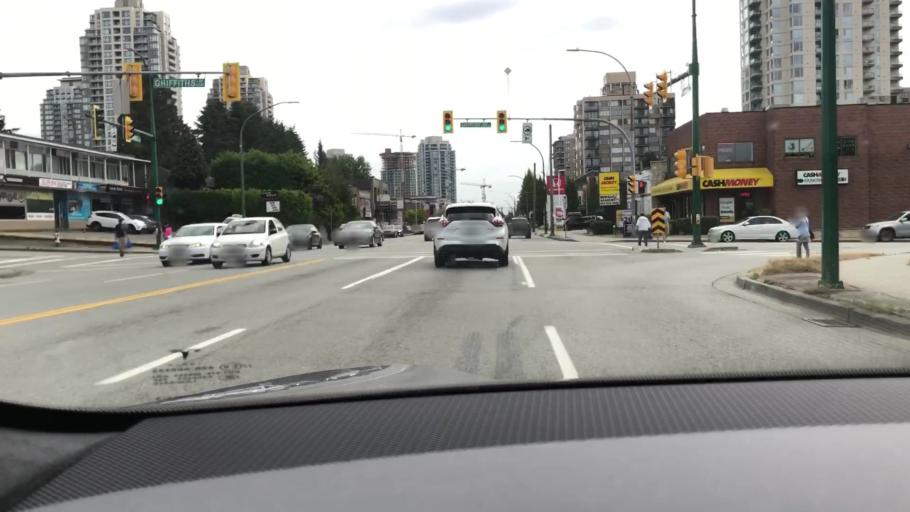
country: CA
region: British Columbia
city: Burnaby
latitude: 49.2036
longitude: -122.9948
